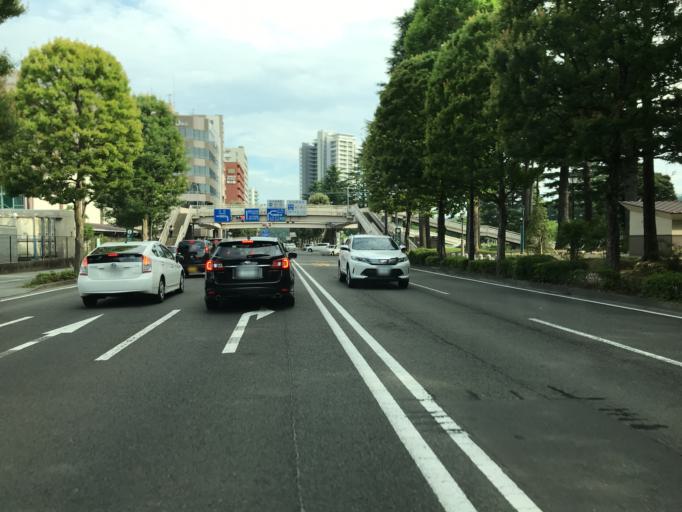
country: JP
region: Miyagi
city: Sendai
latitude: 38.2619
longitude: 140.8630
